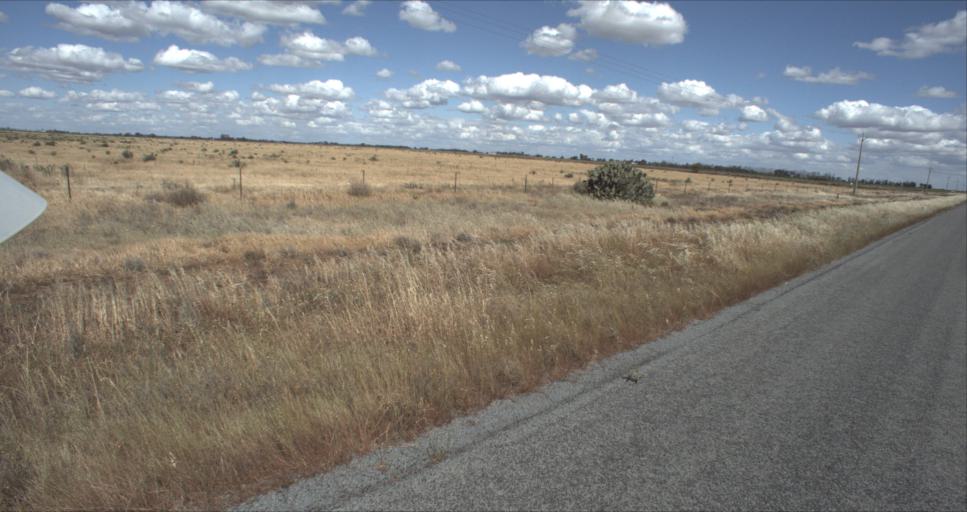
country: AU
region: New South Wales
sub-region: Leeton
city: Leeton
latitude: -34.4956
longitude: 146.2464
